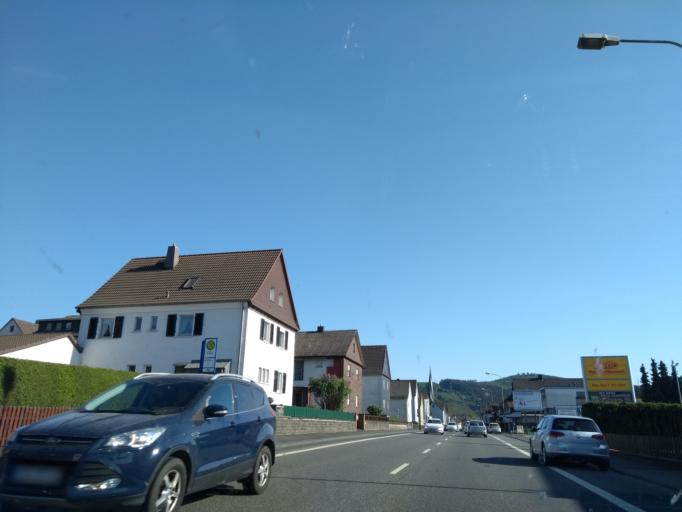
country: DE
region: Hesse
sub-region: Regierungsbezirk Giessen
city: Breidenbach
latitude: 50.8898
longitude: 8.4535
